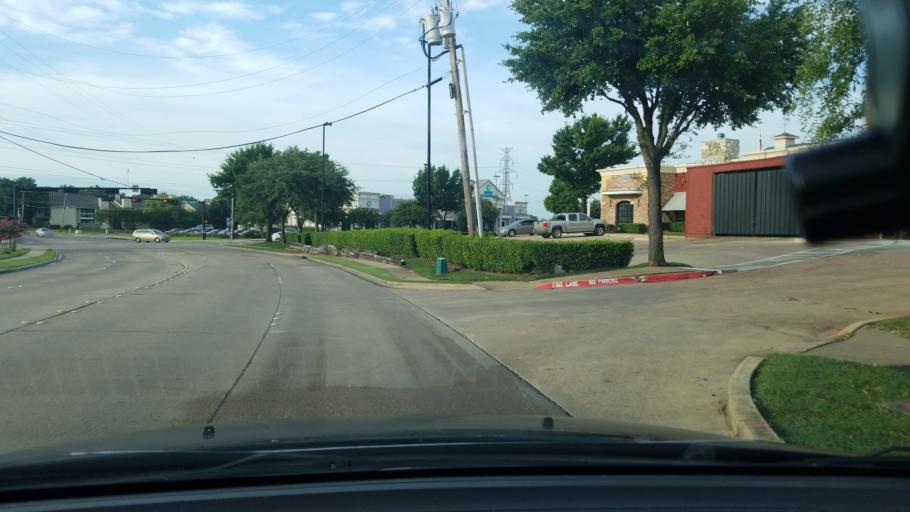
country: US
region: Texas
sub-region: Dallas County
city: Mesquite
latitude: 32.8035
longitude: -96.6248
